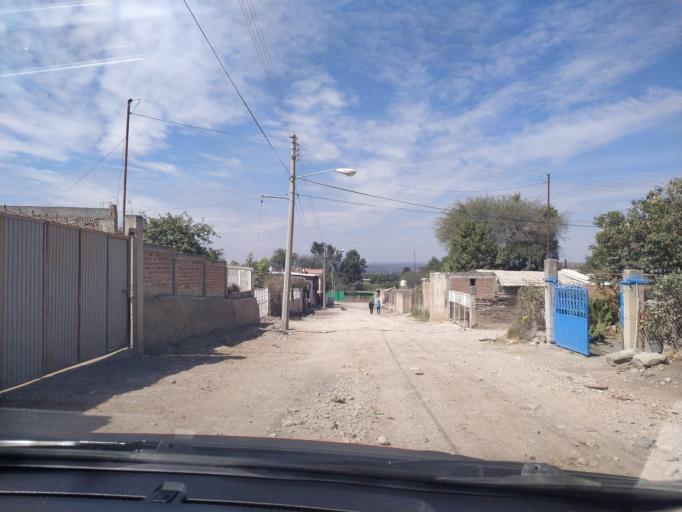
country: MX
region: Guanajuato
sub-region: San Francisco del Rincon
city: San Ignacio de Hidalgo
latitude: 20.8818
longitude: -101.8512
